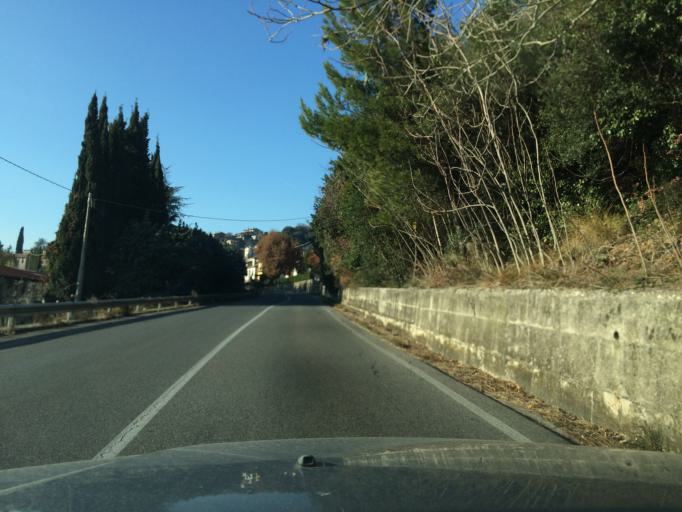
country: IT
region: Umbria
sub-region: Provincia di Terni
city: Fornole
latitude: 42.5424
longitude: 12.4614
